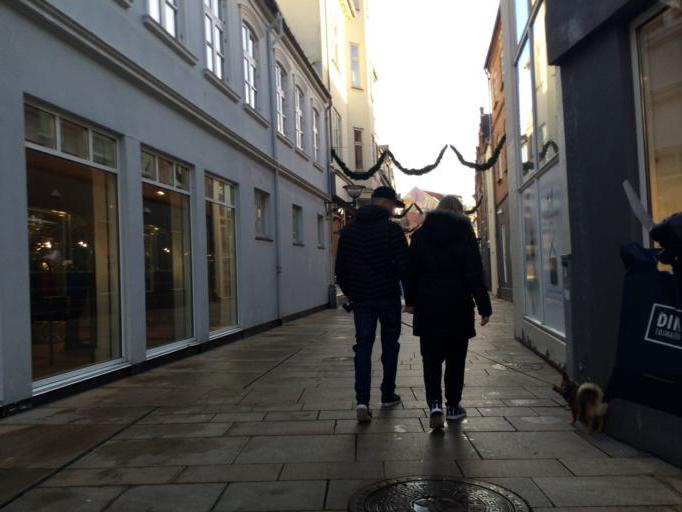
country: DK
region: South Denmark
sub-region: Vejle Kommune
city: Vejle
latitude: 55.7095
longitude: 9.5335
